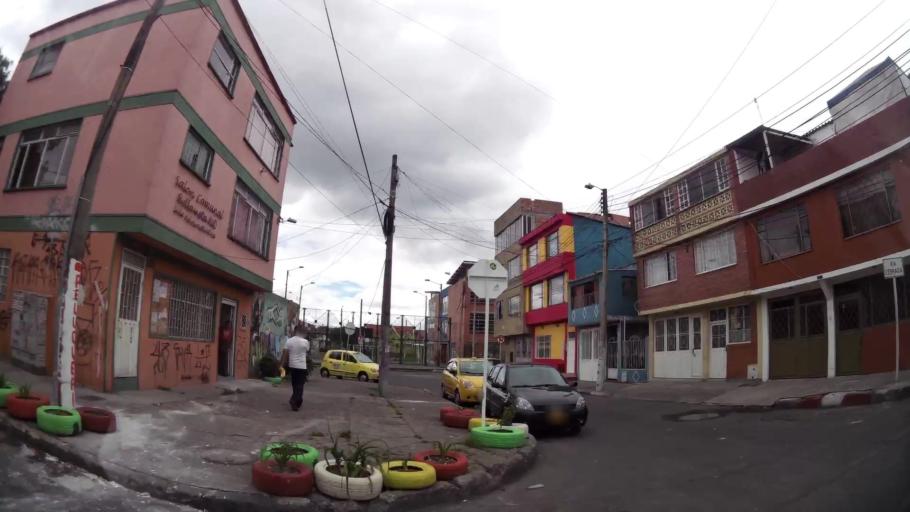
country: CO
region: Bogota D.C.
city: Bogota
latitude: 4.6768
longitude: -74.0900
